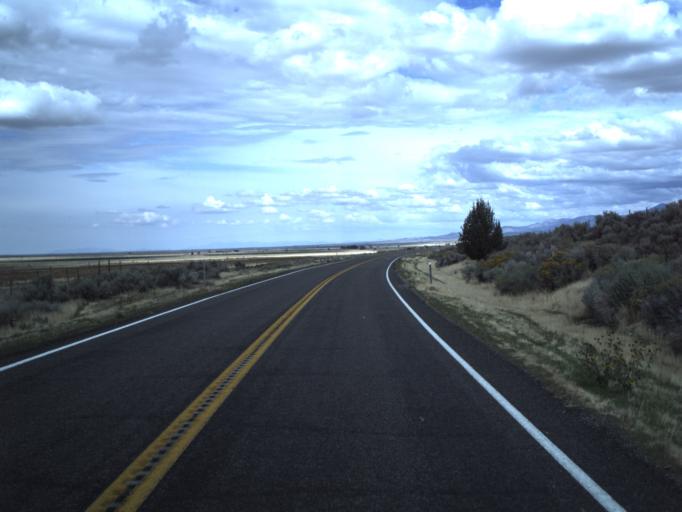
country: US
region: Utah
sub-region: Millard County
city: Fillmore
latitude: 38.9987
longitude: -112.4132
